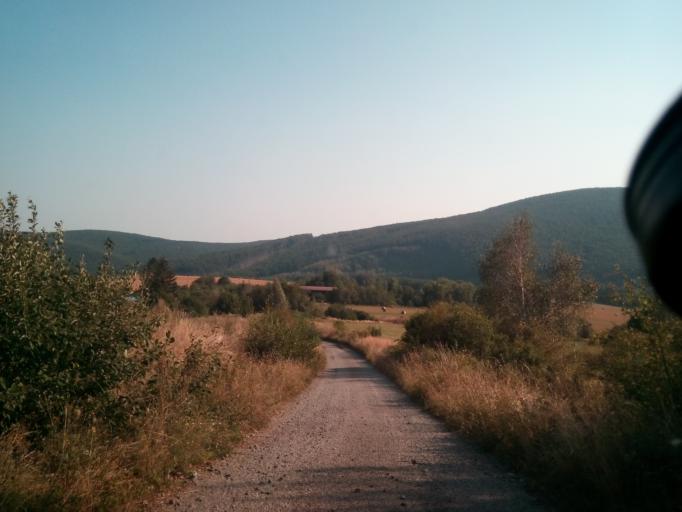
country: SK
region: Kosicky
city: Moldava nad Bodvou
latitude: 48.7314
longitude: 21.1000
